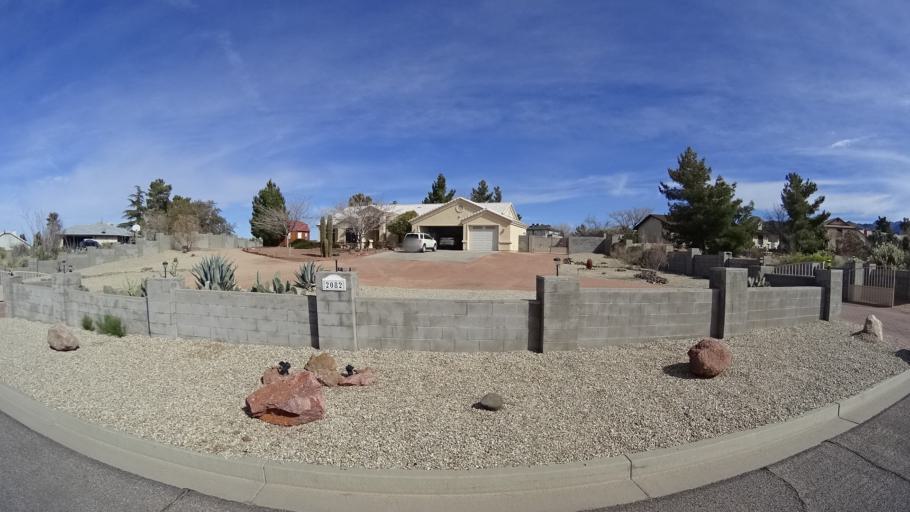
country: US
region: Arizona
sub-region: Mohave County
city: Kingman
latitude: 35.1851
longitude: -113.9901
